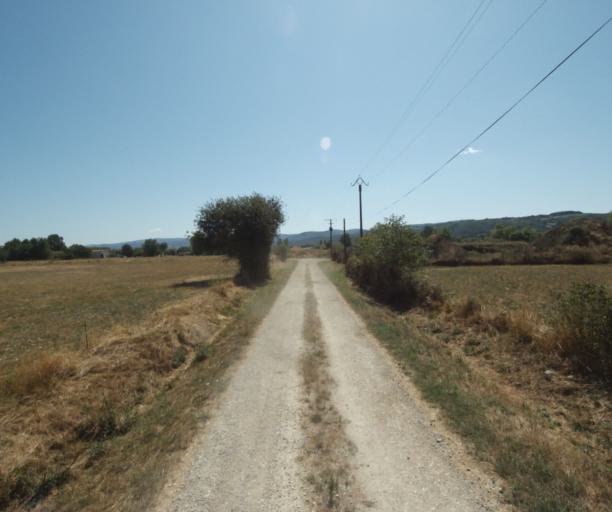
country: FR
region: Midi-Pyrenees
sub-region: Departement de la Haute-Garonne
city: Revel
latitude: 43.4602
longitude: 1.9870
